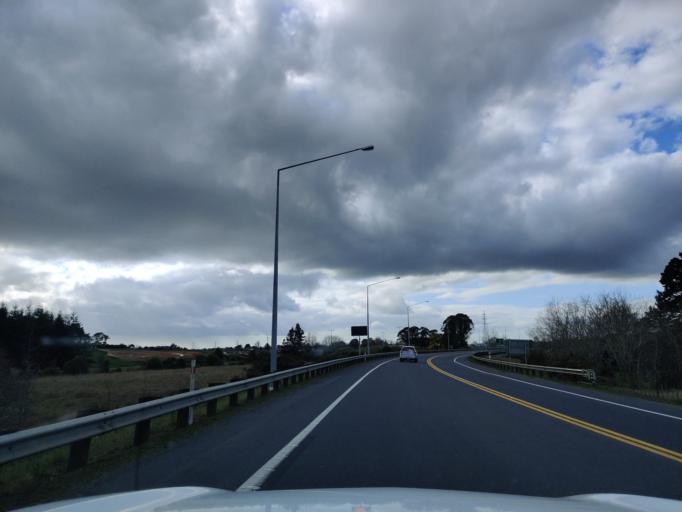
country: NZ
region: Auckland
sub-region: Auckland
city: Papakura
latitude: -37.1114
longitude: 174.9424
